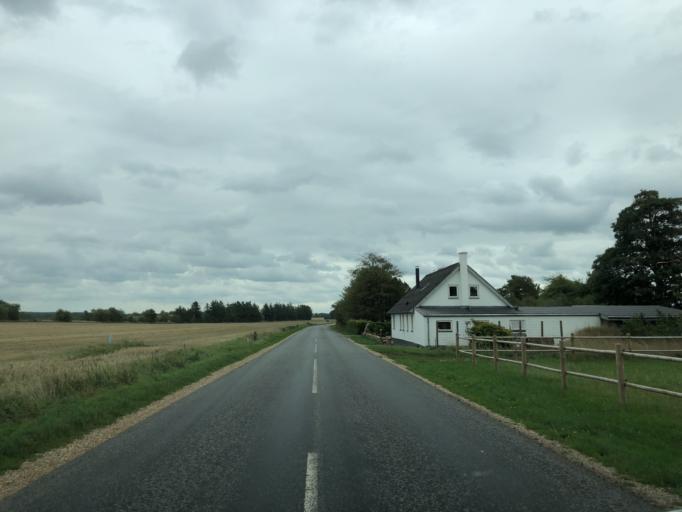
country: DK
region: Central Jutland
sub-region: Herning Kommune
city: Lind
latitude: 56.0899
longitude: 8.9346
